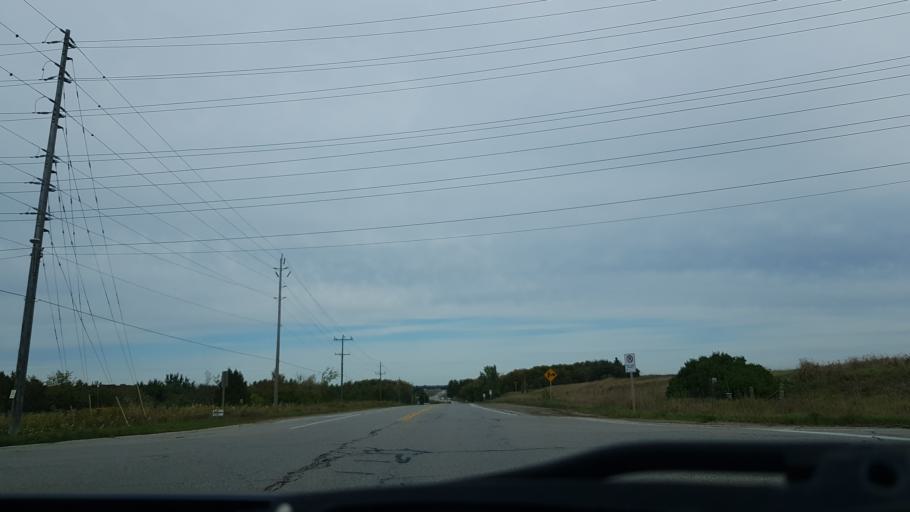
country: CA
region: Ontario
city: Orangeville
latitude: 43.8106
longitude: -80.0502
